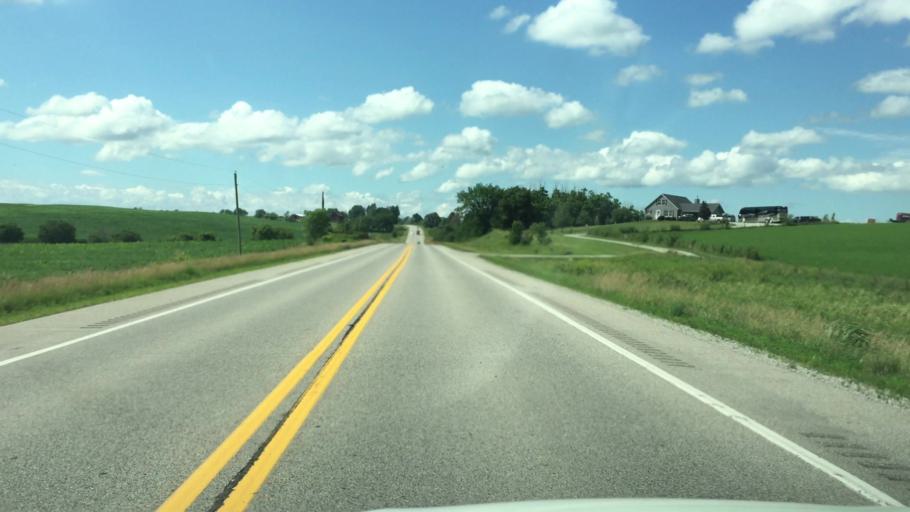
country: US
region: Iowa
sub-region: Johnson County
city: Solon
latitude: 41.7515
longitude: -91.4744
